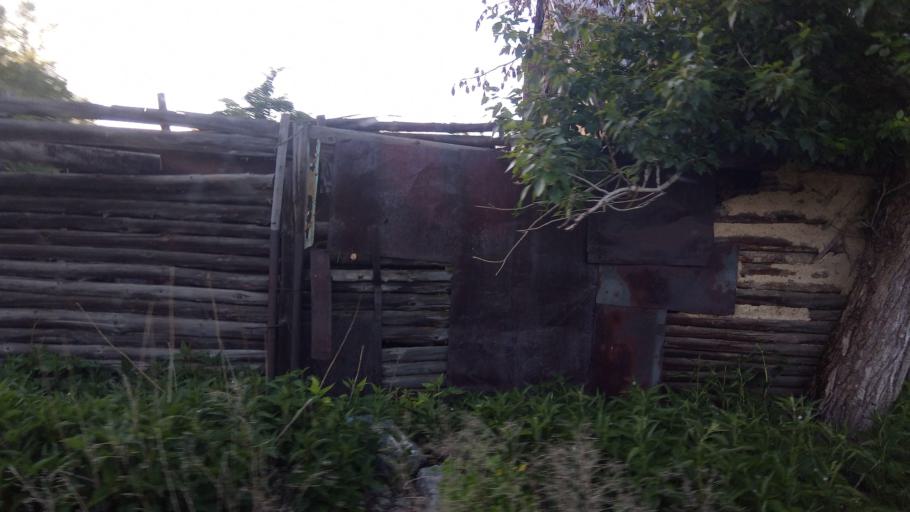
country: RU
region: Chelyabinsk
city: Timiryazevskiy
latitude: 54.9872
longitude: 60.8423
